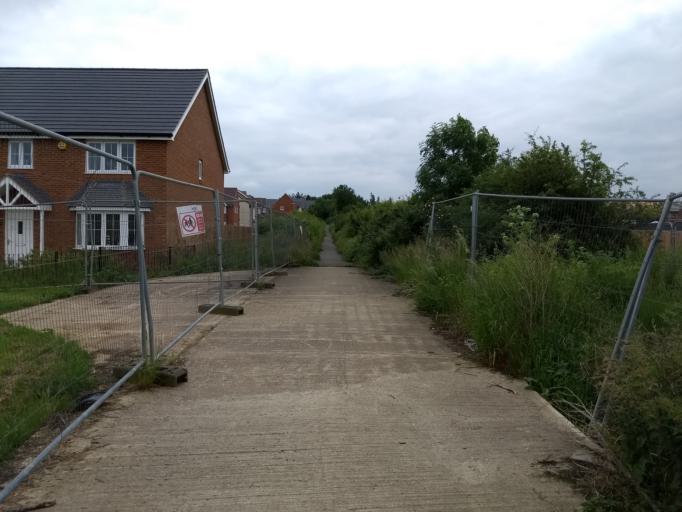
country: GB
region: England
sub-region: Central Bedfordshire
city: Marston Moretaine
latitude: 52.0641
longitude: -0.5585
